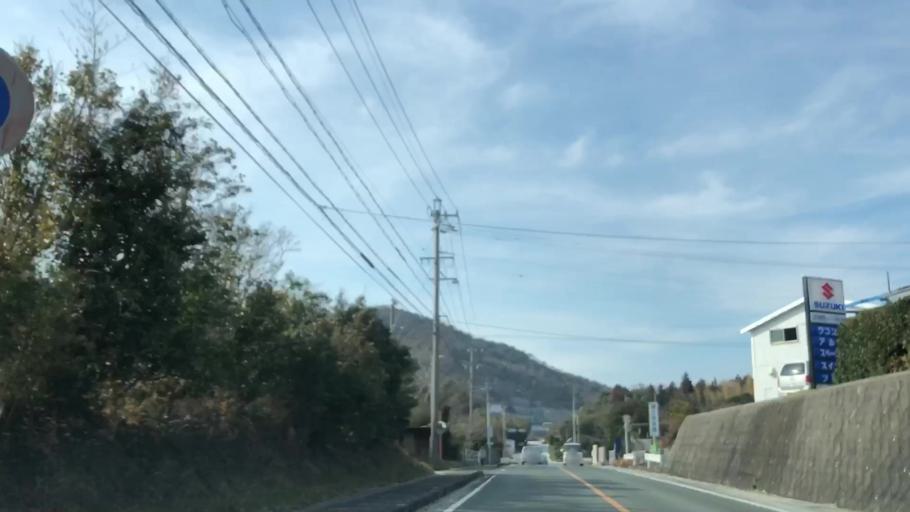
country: JP
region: Aichi
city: Tahara
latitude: 34.6783
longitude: 137.2516
